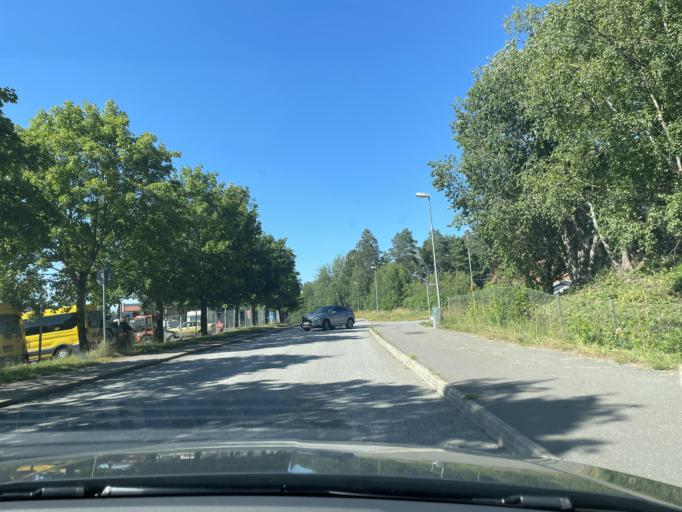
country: SE
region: Stockholm
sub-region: Sigtuna Kommun
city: Rosersberg
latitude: 59.5846
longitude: 17.8816
